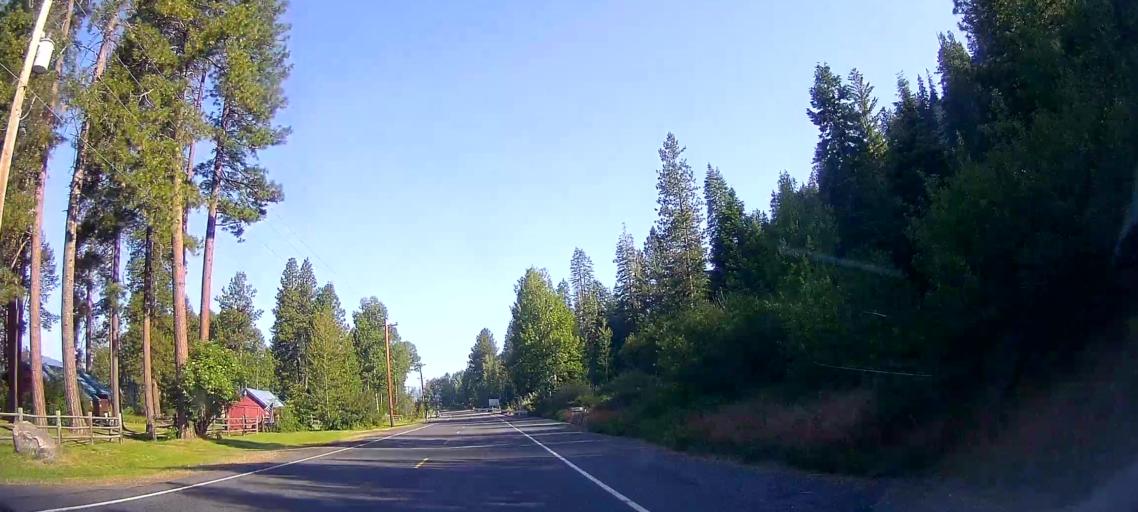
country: US
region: Oregon
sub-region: Klamath County
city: Klamath Falls
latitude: 42.6407
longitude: -121.9424
